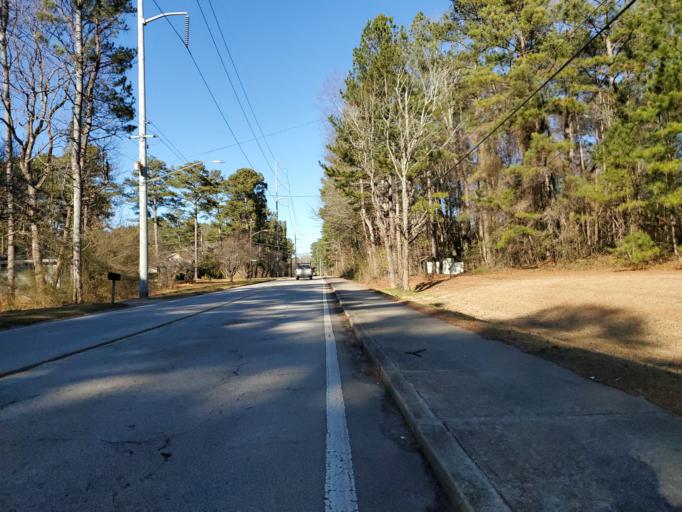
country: US
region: Georgia
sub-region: DeKalb County
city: Stone Mountain
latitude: 33.7782
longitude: -84.2050
